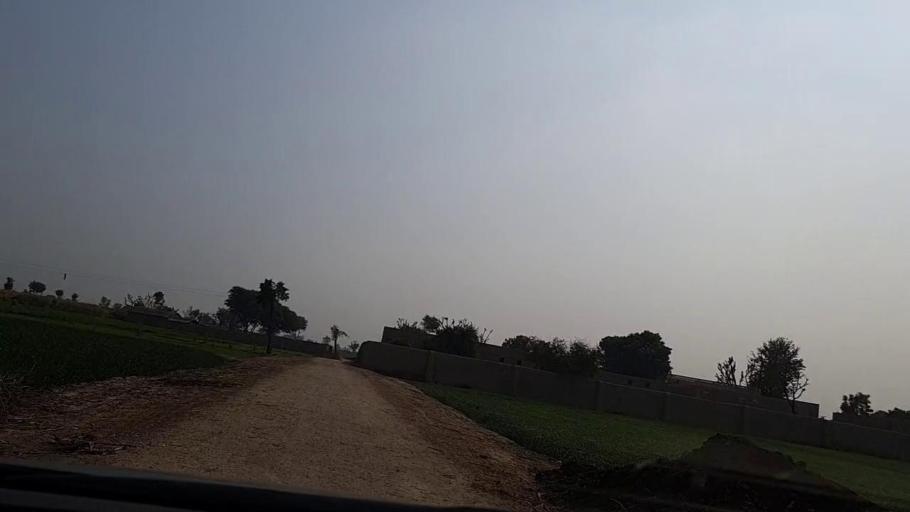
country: PK
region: Sindh
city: Sakrand
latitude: 26.1442
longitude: 68.2335
